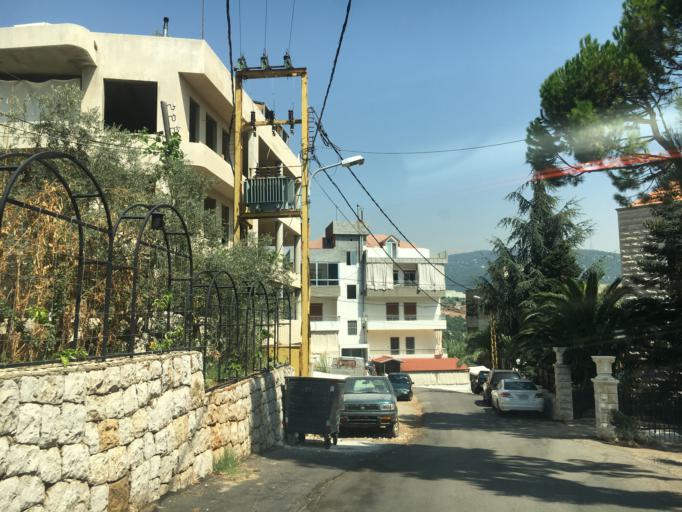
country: LB
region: Mont-Liban
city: Djounie
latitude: 33.9526
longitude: 35.6975
